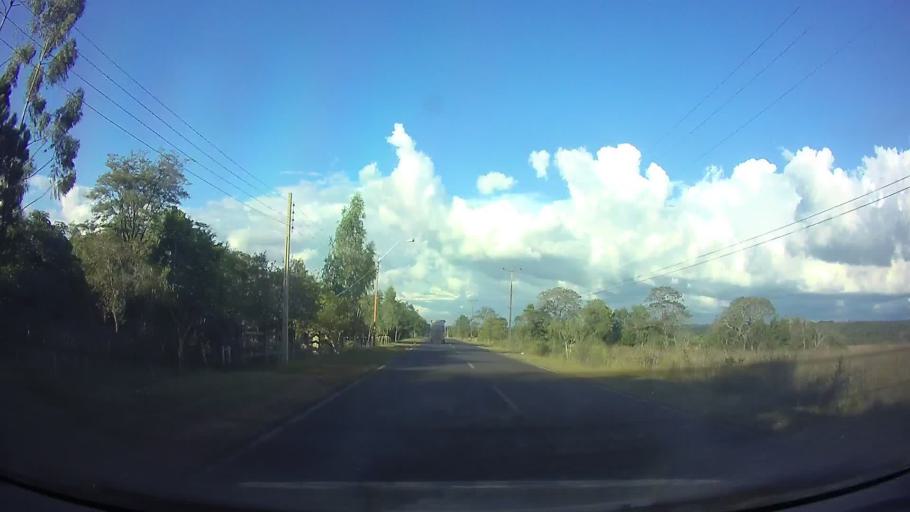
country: PY
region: Cordillera
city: Emboscada
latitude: -25.1650
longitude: -57.2694
